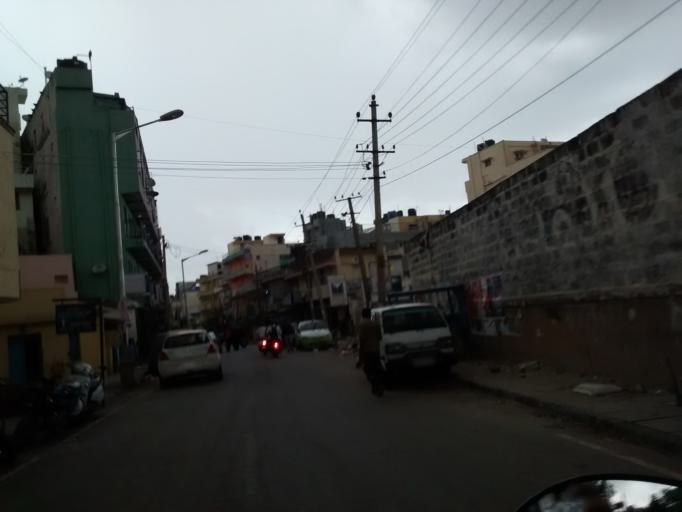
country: IN
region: Karnataka
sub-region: Bangalore Urban
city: Bangalore
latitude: 12.9207
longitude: 77.6119
